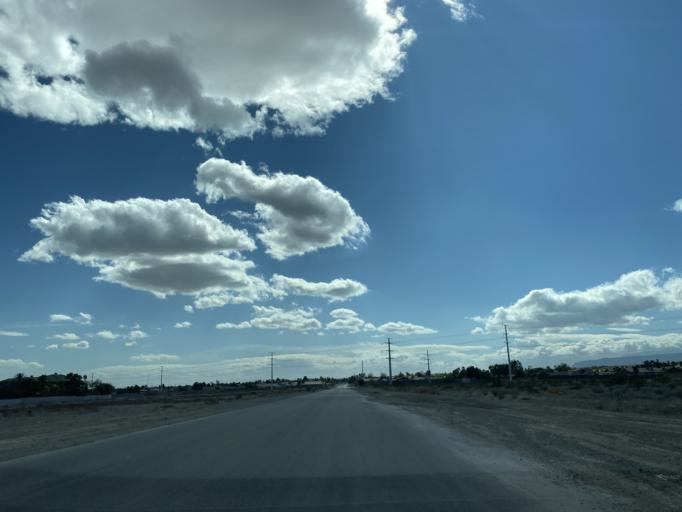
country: US
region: Nevada
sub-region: Clark County
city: Summerlin South
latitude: 36.2445
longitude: -115.2884
